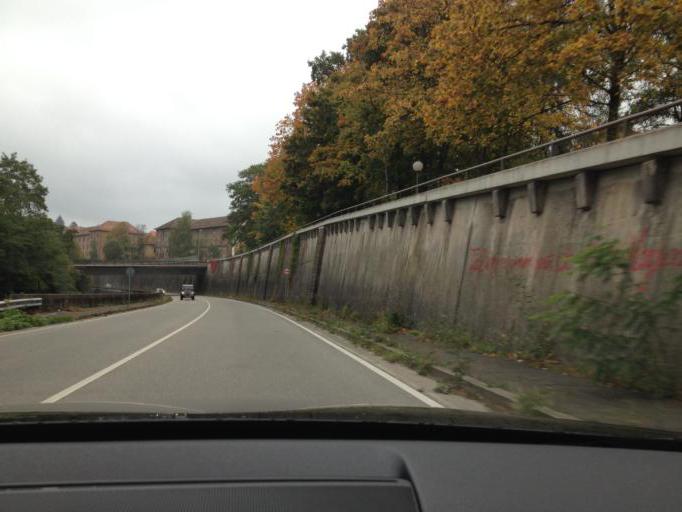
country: DE
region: Rheinland-Pfalz
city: Zweibrucken
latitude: 49.2426
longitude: 7.3658
